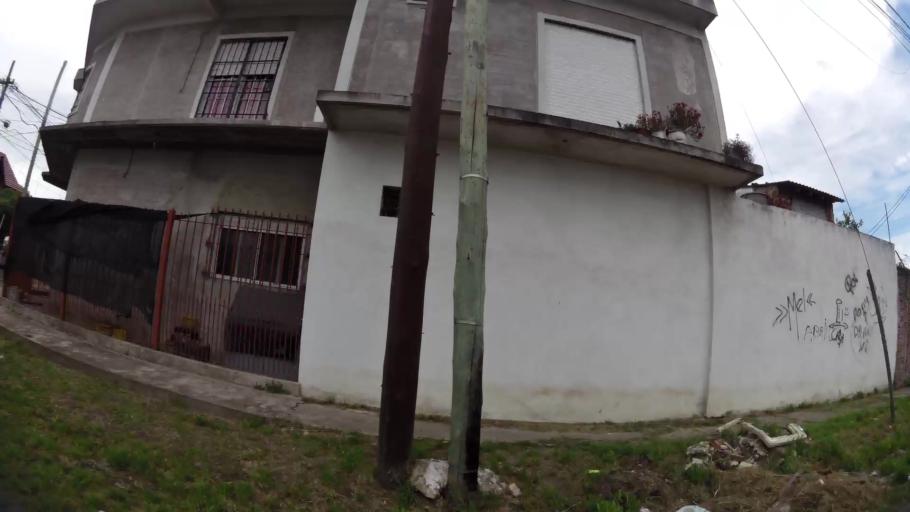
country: AR
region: Buenos Aires
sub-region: Partido de Quilmes
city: Quilmes
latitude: -34.7581
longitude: -58.2359
